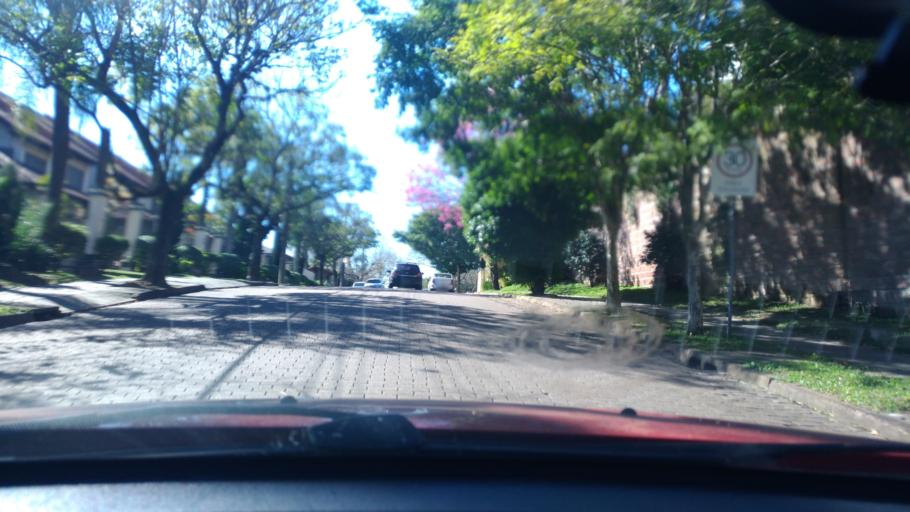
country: BR
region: Rio Grande do Sul
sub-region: Porto Alegre
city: Porto Alegre
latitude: -30.0340
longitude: -51.1477
